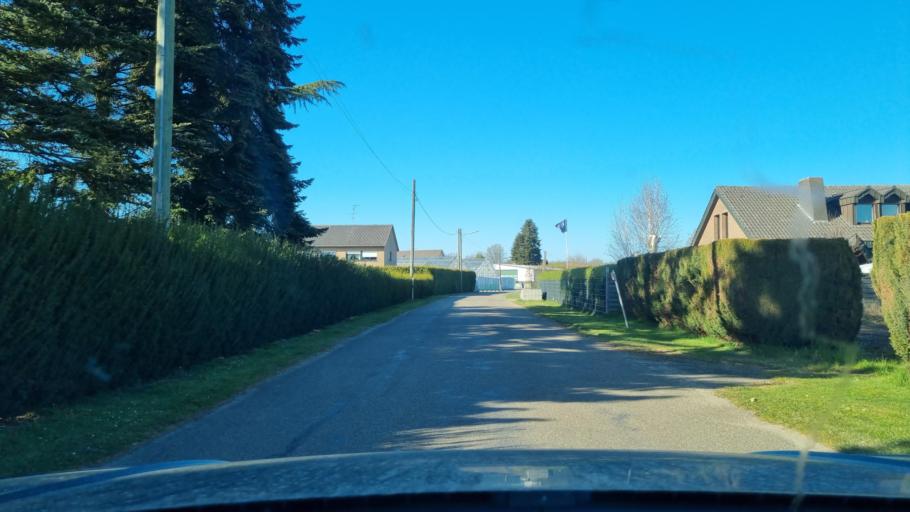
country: DE
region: North Rhine-Westphalia
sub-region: Regierungsbezirk Dusseldorf
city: Goch
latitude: 51.7192
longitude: 6.1370
